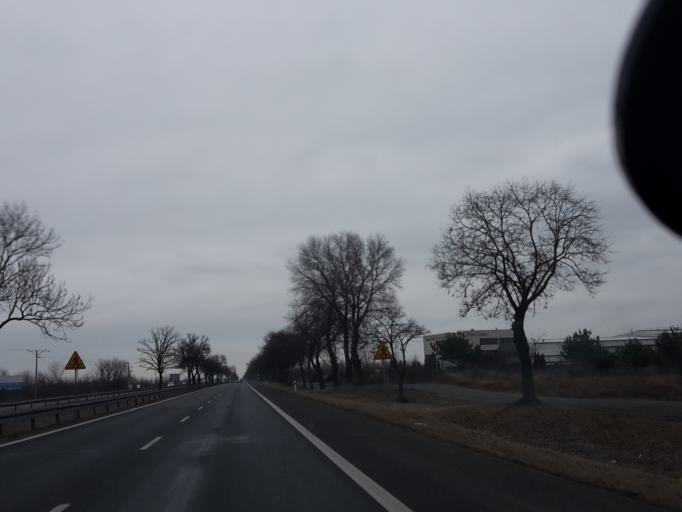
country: PL
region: Masovian Voivodeship
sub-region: Powiat nowodworski
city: Nowy Dwor Mazowiecki
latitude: 52.3808
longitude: 20.7626
